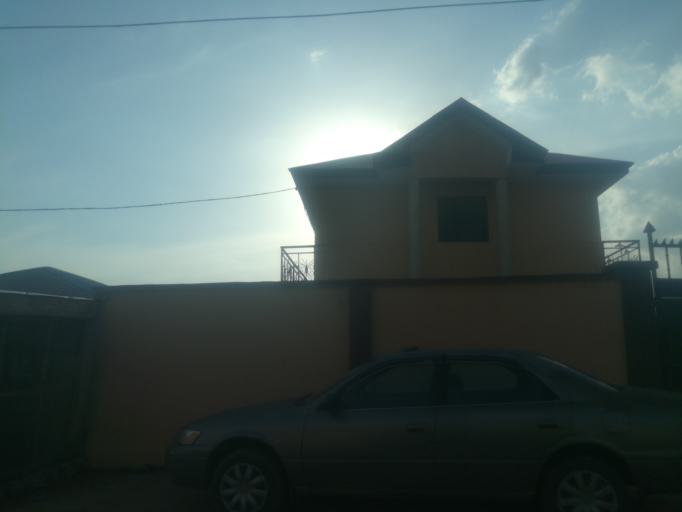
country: NG
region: Ogun
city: Abeokuta
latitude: 7.1169
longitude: 3.3267
